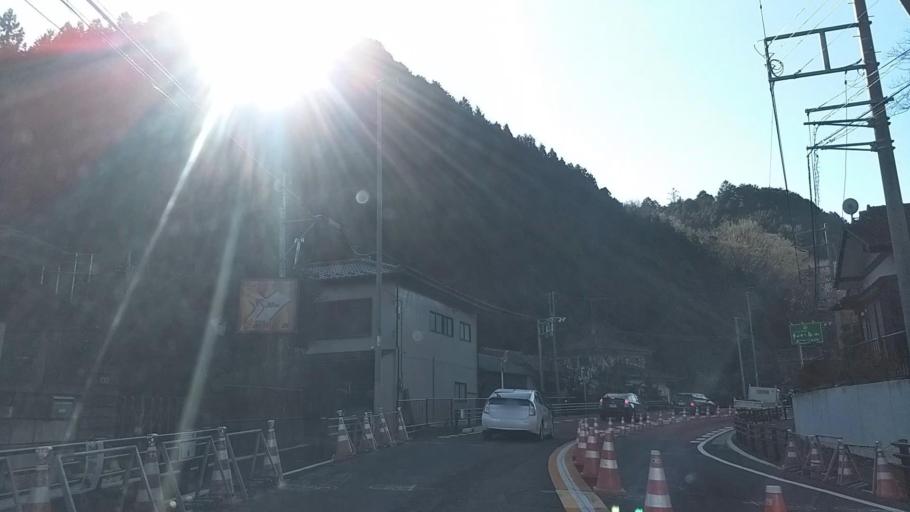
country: JP
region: Tokyo
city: Hachioji
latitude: 35.6184
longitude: 139.2626
